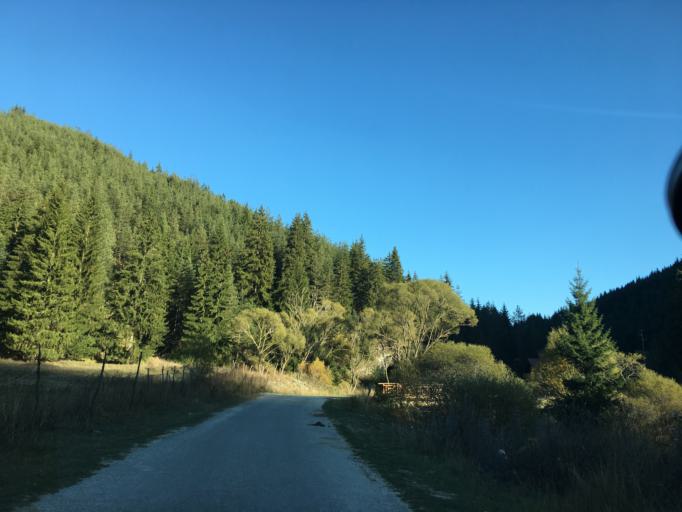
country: BG
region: Smolyan
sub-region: Obshtina Borino
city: Borino
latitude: 41.5826
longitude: 24.3946
